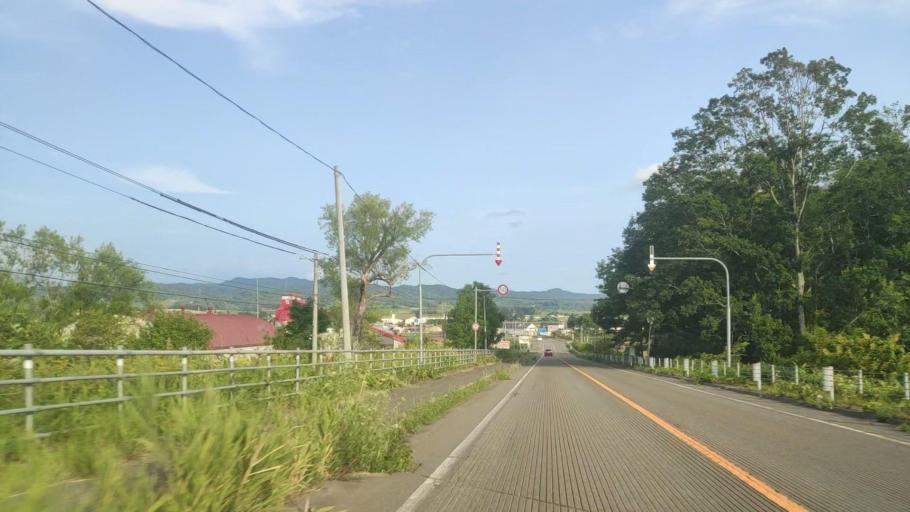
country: JP
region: Hokkaido
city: Iwamizawa
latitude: 43.0221
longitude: 141.8505
